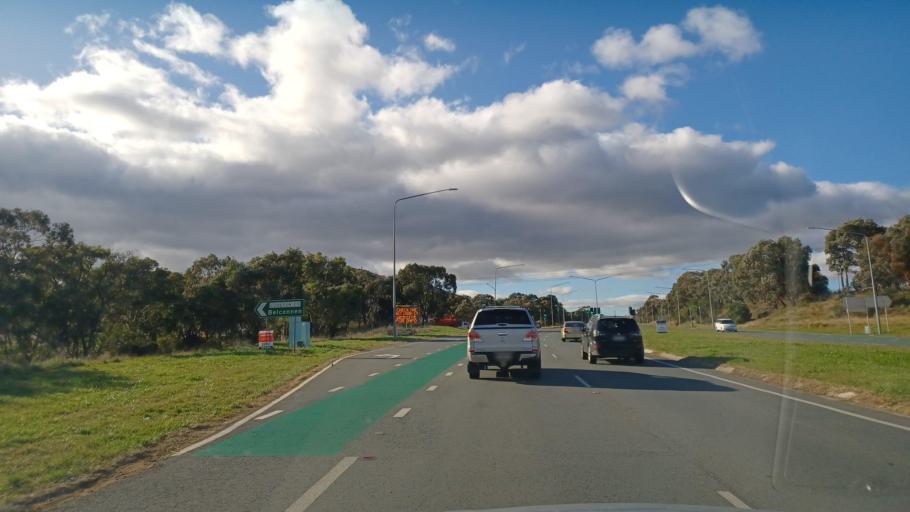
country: AU
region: Australian Capital Territory
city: Macquarie
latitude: -35.2693
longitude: 149.0516
